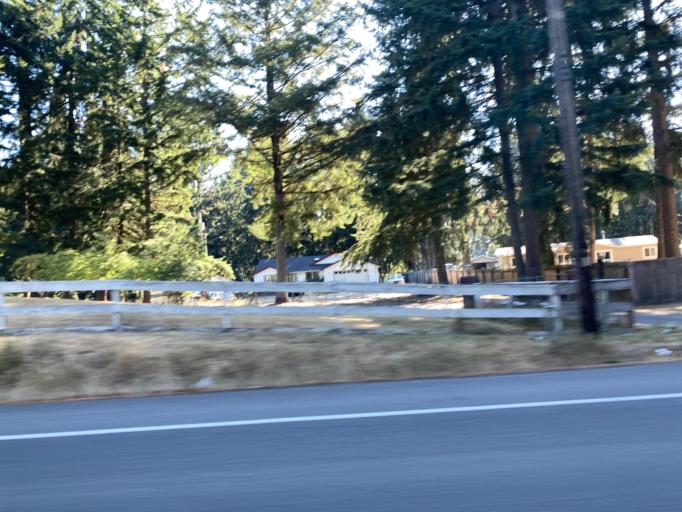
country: US
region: Washington
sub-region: Thurston County
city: Tanglewilde-Thompson Place
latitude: 47.0048
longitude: -122.7386
